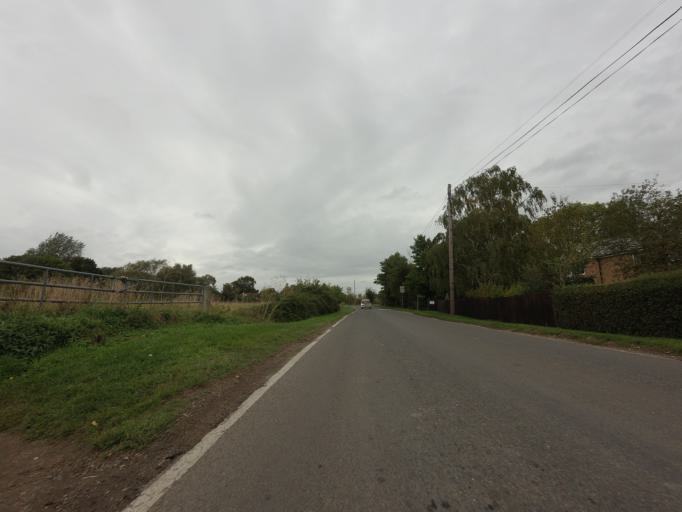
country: GB
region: England
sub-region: Cambridgeshire
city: Harston
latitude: 52.0960
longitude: 0.0697
